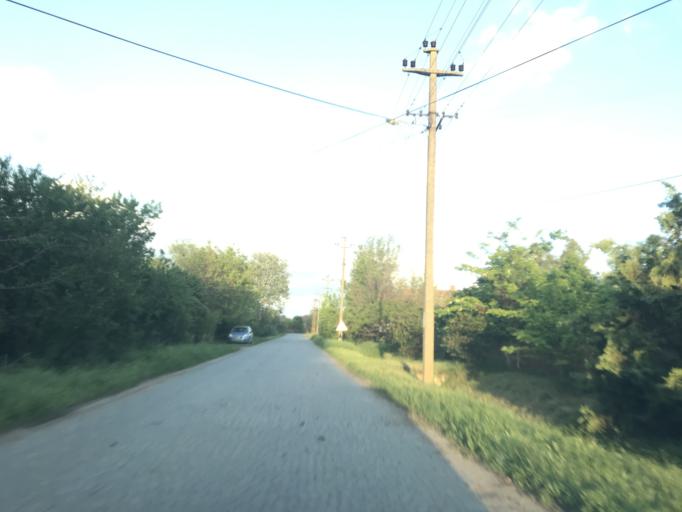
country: RS
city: Banatski Dvor
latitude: 45.5202
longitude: 20.5044
